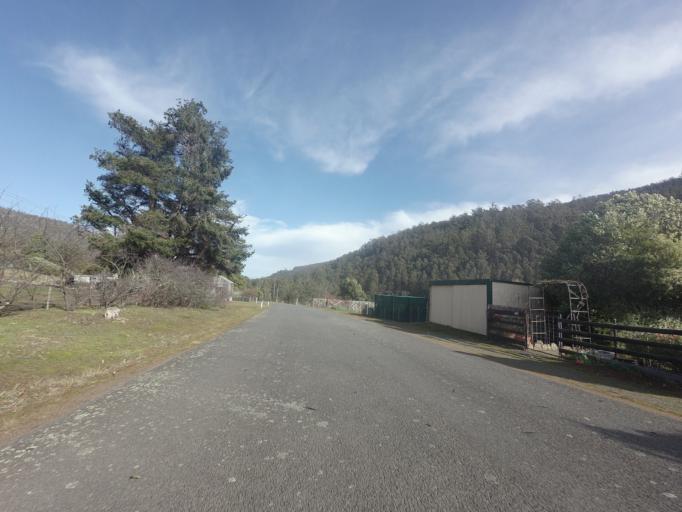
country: AU
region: Tasmania
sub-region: Huon Valley
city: Huonville
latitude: -43.0471
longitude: 147.1122
